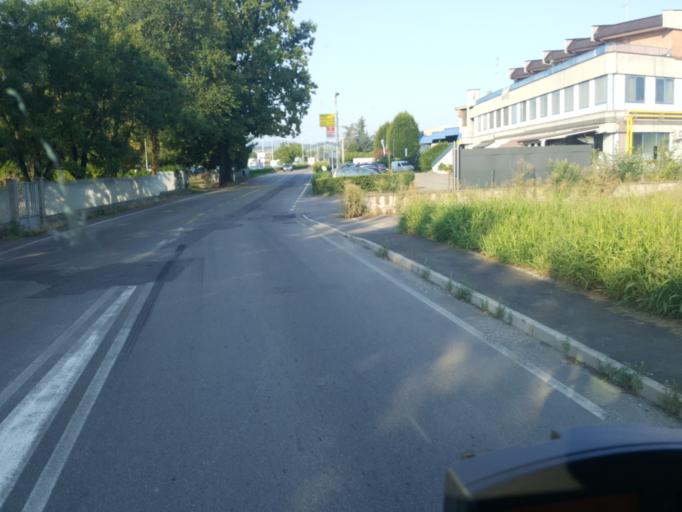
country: IT
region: Emilia-Romagna
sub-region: Provincia di Modena
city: Ca' di Sola
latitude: 44.5311
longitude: 10.9814
